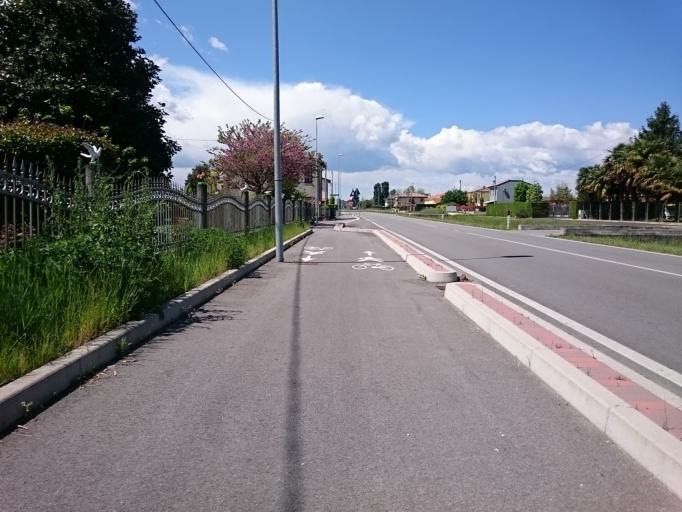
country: IT
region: Veneto
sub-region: Provincia di Padova
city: Bertipaglia
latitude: 45.3138
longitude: 11.8931
